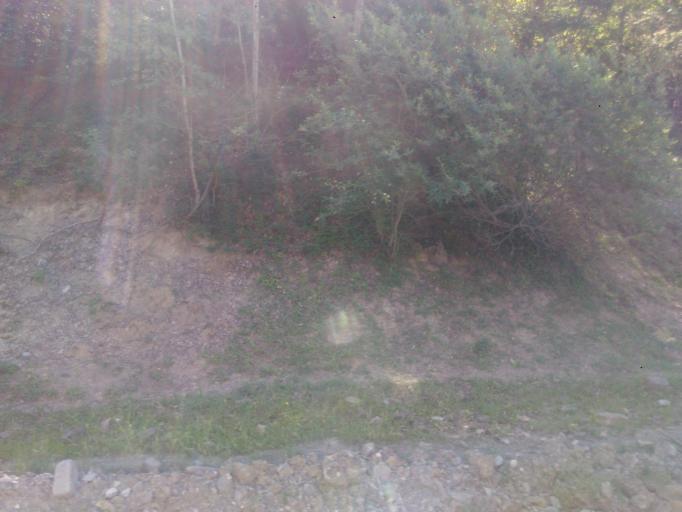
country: GE
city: Zhinvali
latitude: 42.1891
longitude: 44.8216
